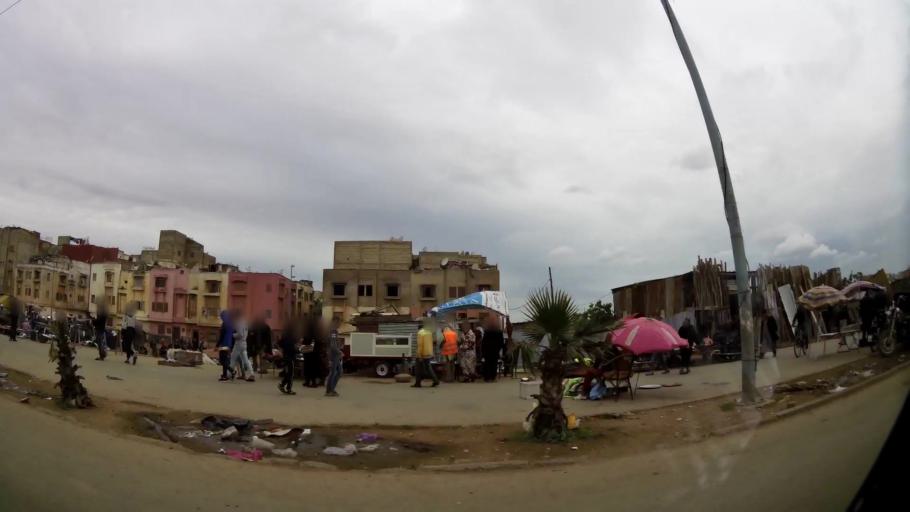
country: MA
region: Grand Casablanca
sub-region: Mediouna
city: Tit Mellil
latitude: 33.5593
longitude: -7.5460
